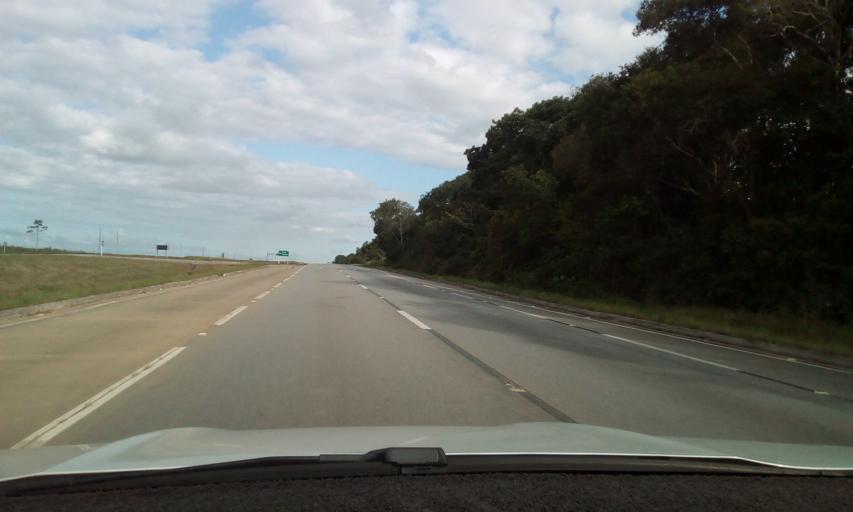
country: BR
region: Paraiba
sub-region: Cruz Do Espirito Santo
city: Cruz do Espirito Santo
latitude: -7.0307
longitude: -35.0578
